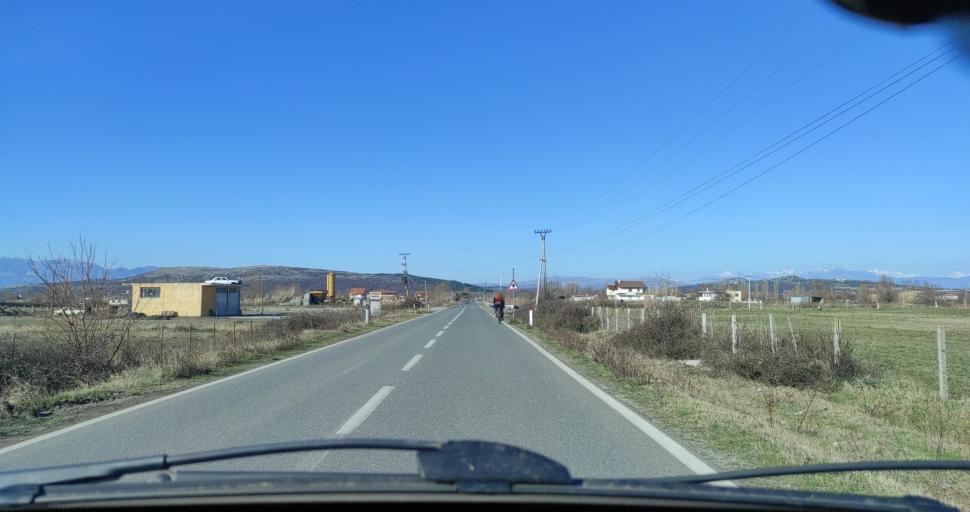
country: AL
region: Shkoder
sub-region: Rrethi i Shkodres
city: Velipoje
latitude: 41.8851
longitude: 19.4036
